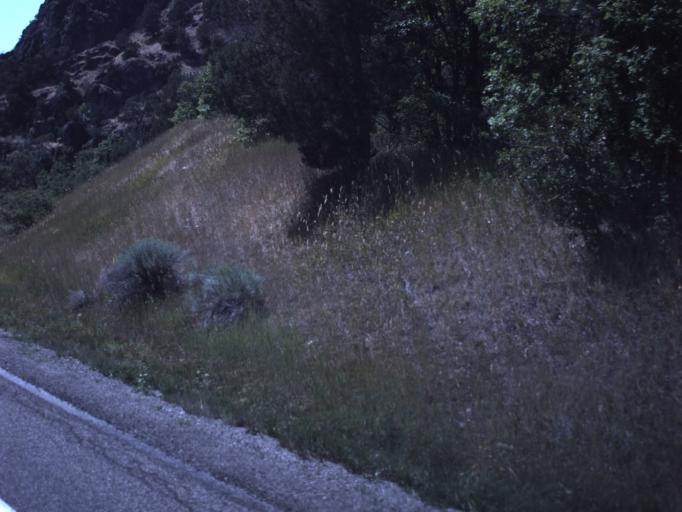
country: US
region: Utah
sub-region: Cache County
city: North Logan
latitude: 41.7690
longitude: -111.6615
